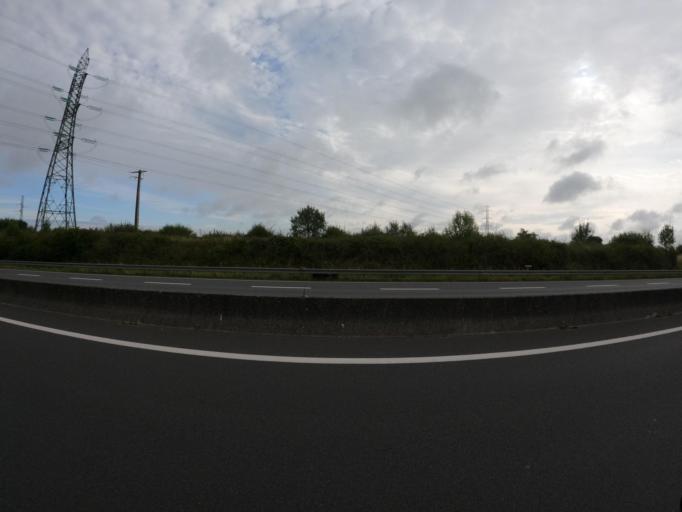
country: FR
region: Centre
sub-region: Departement d'Indre-et-Loire
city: Villandry
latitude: 47.3139
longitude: 0.5064
